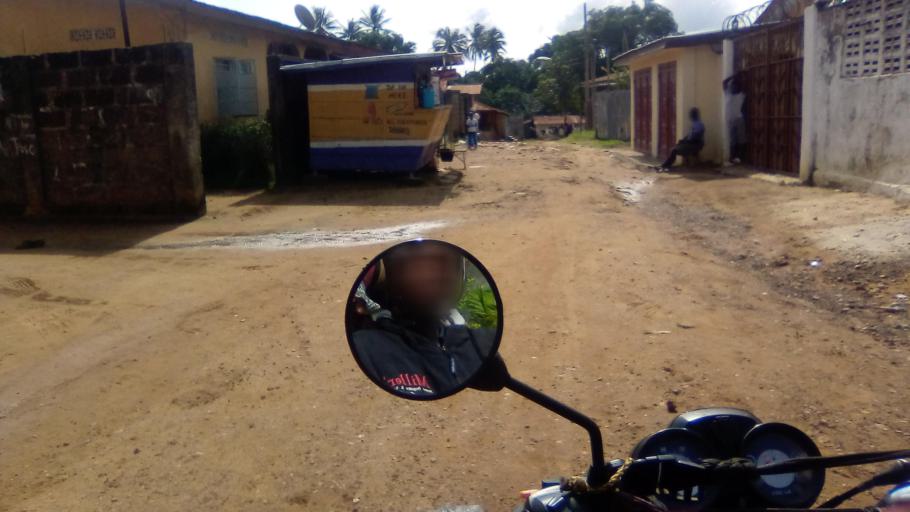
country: SL
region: Southern Province
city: Bo
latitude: 7.9571
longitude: -11.7522
